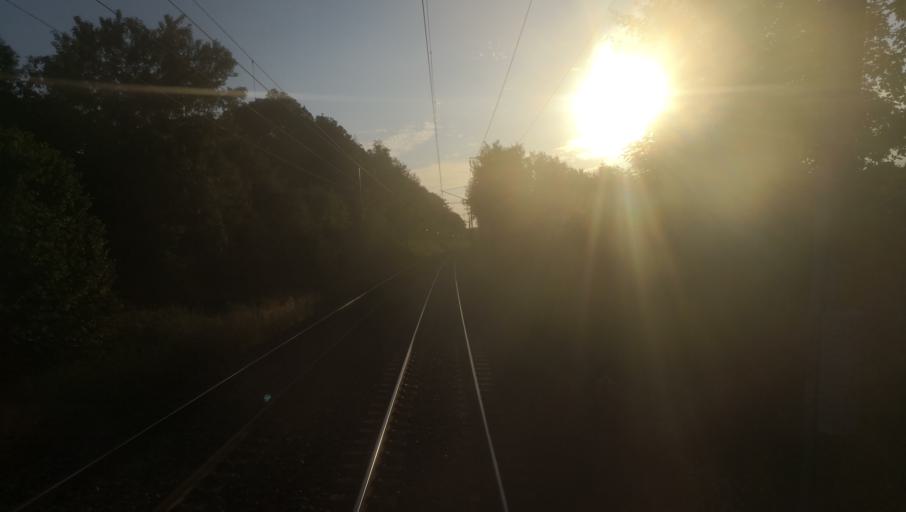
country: FR
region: Lower Normandy
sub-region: Departement du Calvados
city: Beuvillers
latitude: 49.1236
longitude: 0.3018
